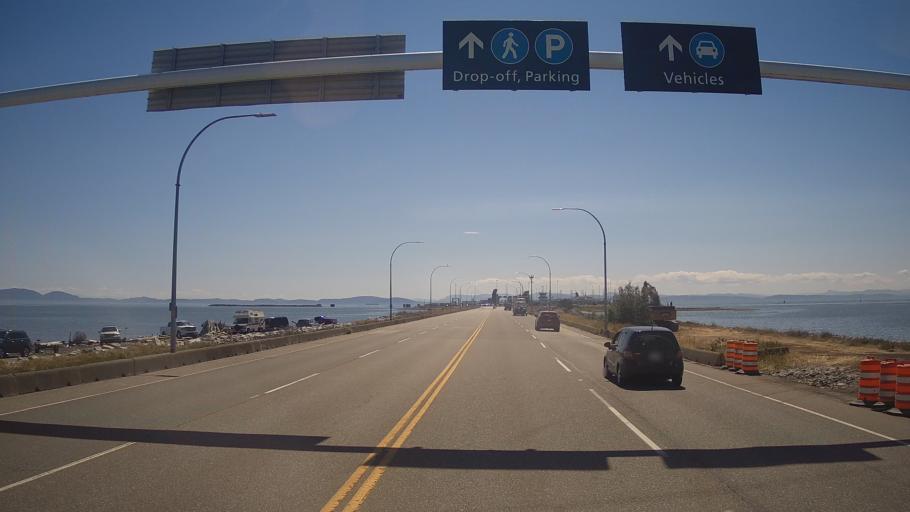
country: US
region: Washington
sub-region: Whatcom County
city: Point Roberts
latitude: 49.0167
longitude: -123.1161
